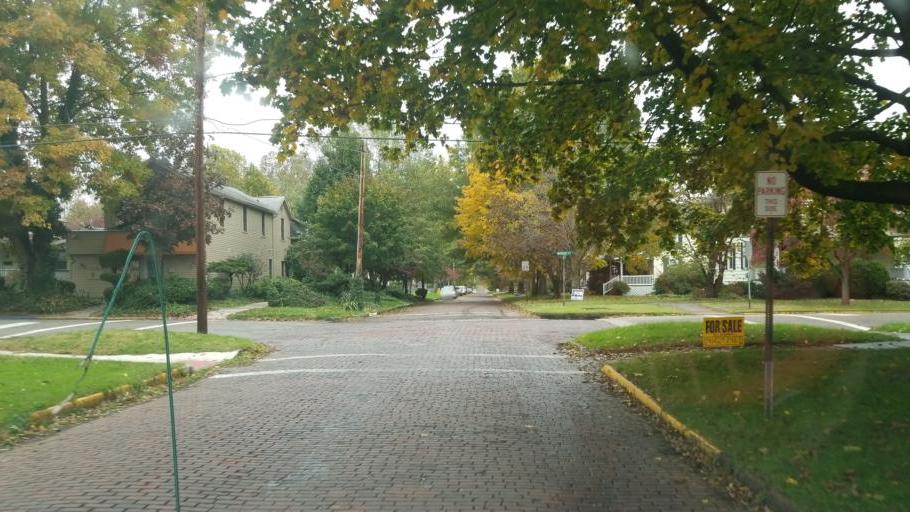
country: US
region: Ohio
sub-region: Washington County
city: Marietta
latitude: 39.4271
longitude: -81.4561
